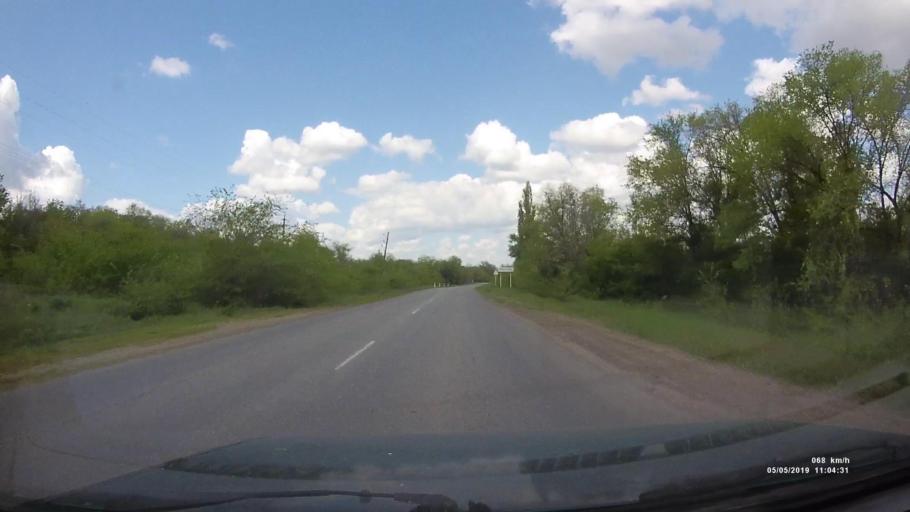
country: RU
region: Rostov
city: Ust'-Donetskiy
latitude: 47.6978
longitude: 40.9172
